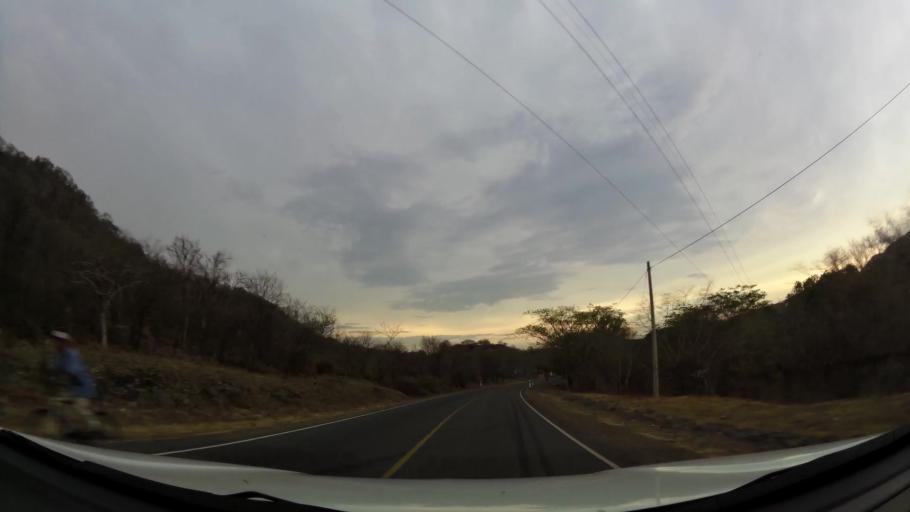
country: NI
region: Leon
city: La Jicaral
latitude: 12.6932
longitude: -86.4084
